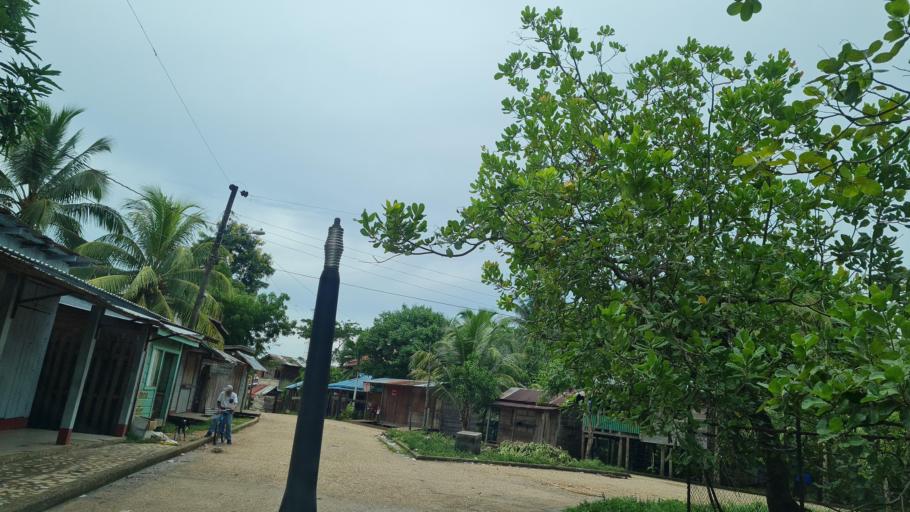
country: NI
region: Atlantico Norte (RAAN)
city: Waspam
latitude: 14.7374
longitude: -83.9700
